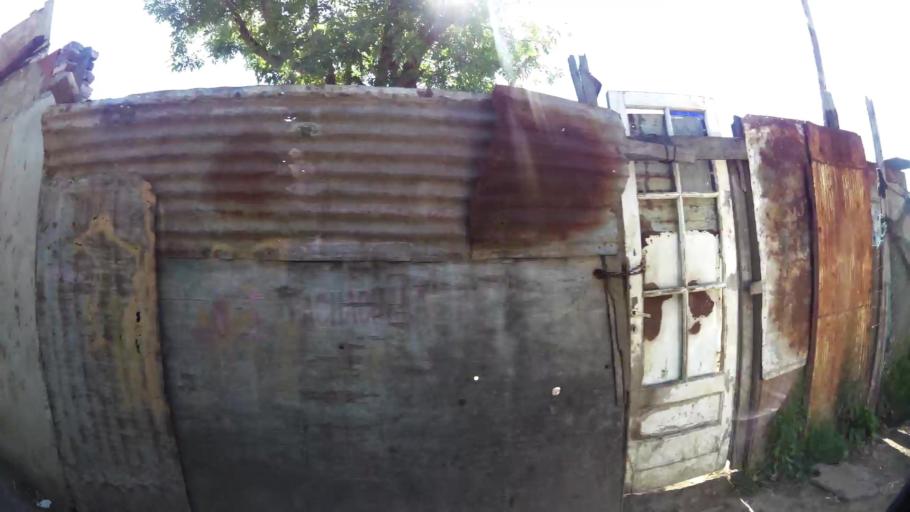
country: AR
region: Santa Fe
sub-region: Departamento de Rosario
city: Rosario
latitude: -32.9746
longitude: -60.6906
